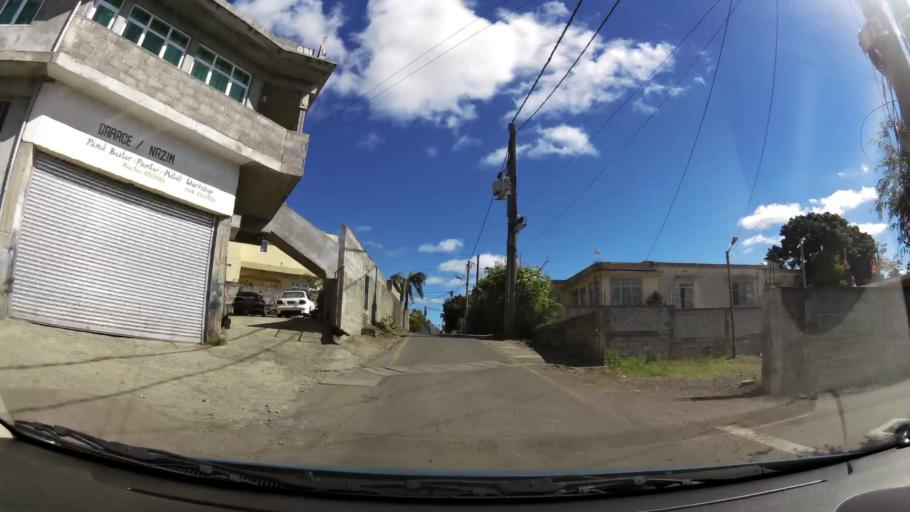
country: MU
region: Plaines Wilhems
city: Vacoas
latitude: -20.3063
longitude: 57.4814
